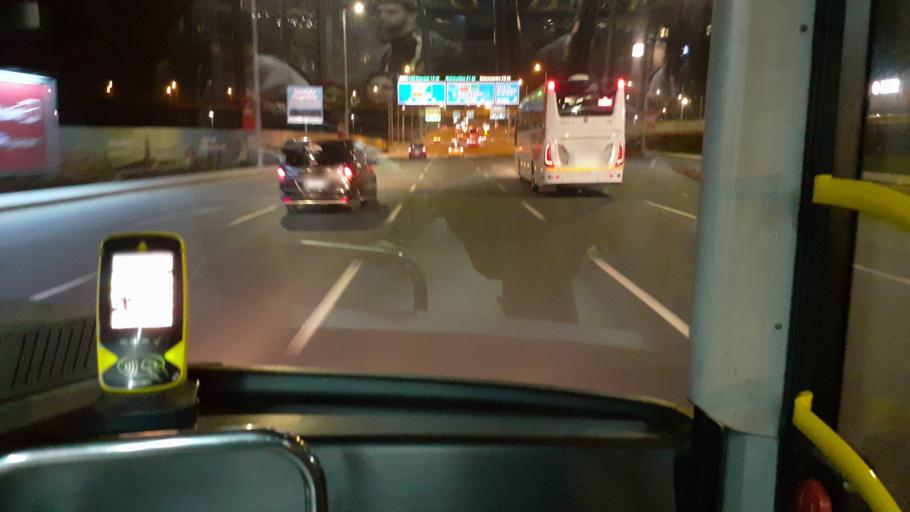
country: TR
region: Istanbul
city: Durusu
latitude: 41.2506
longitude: 28.7389
